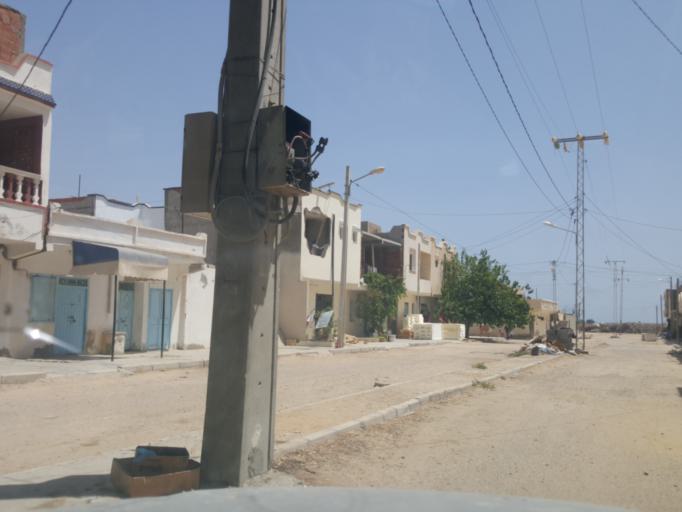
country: TN
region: Safaqis
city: Skhira
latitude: 34.1058
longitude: 9.9833
